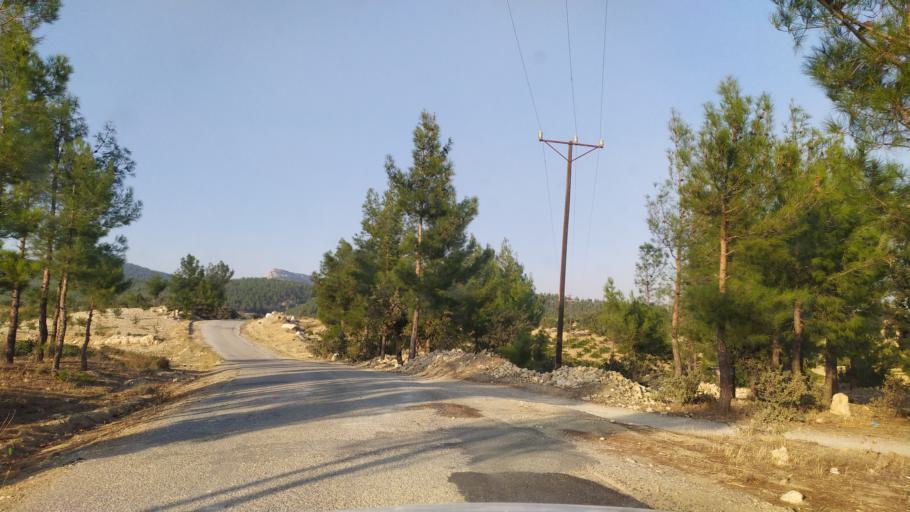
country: TR
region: Mersin
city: Mut
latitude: 36.6888
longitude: 33.1976
